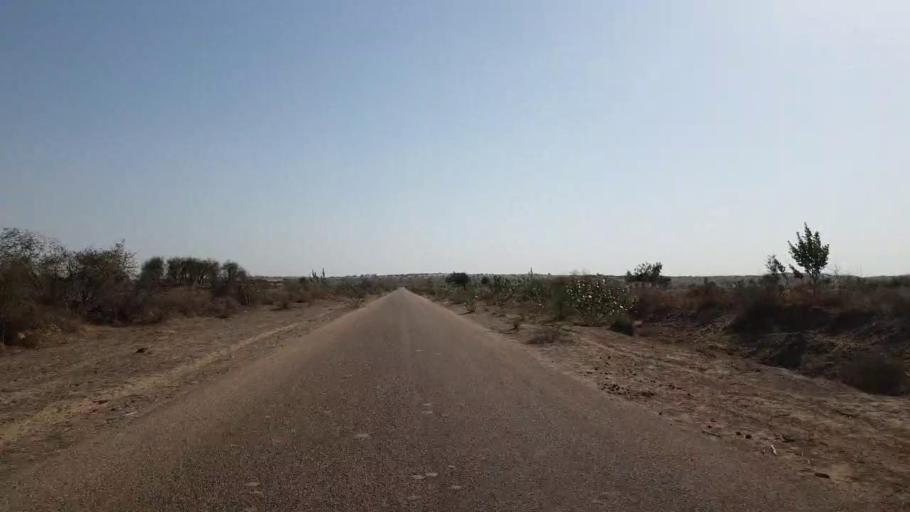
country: PK
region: Sindh
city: Islamkot
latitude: 25.0716
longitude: 70.0426
